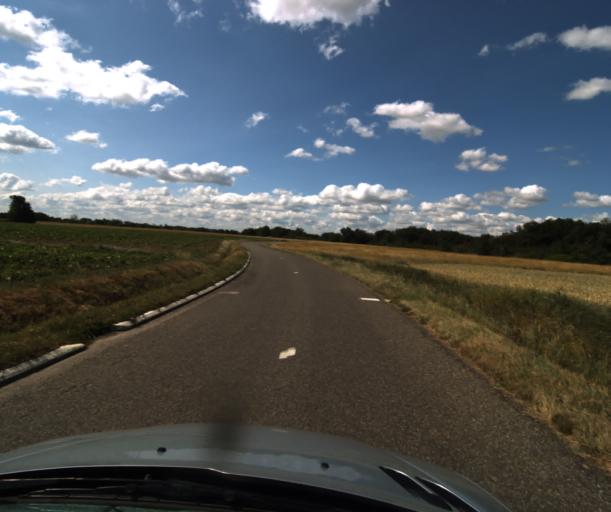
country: FR
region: Midi-Pyrenees
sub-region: Departement du Tarn-et-Garonne
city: Finhan
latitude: 43.9083
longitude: 1.2705
